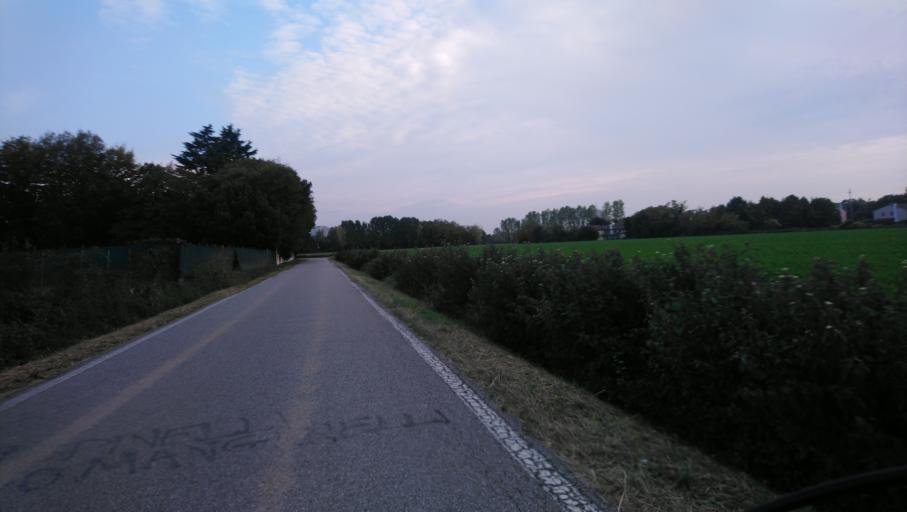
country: IT
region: Veneto
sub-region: Provincia di Treviso
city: Treviso
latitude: 45.6913
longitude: 12.2389
